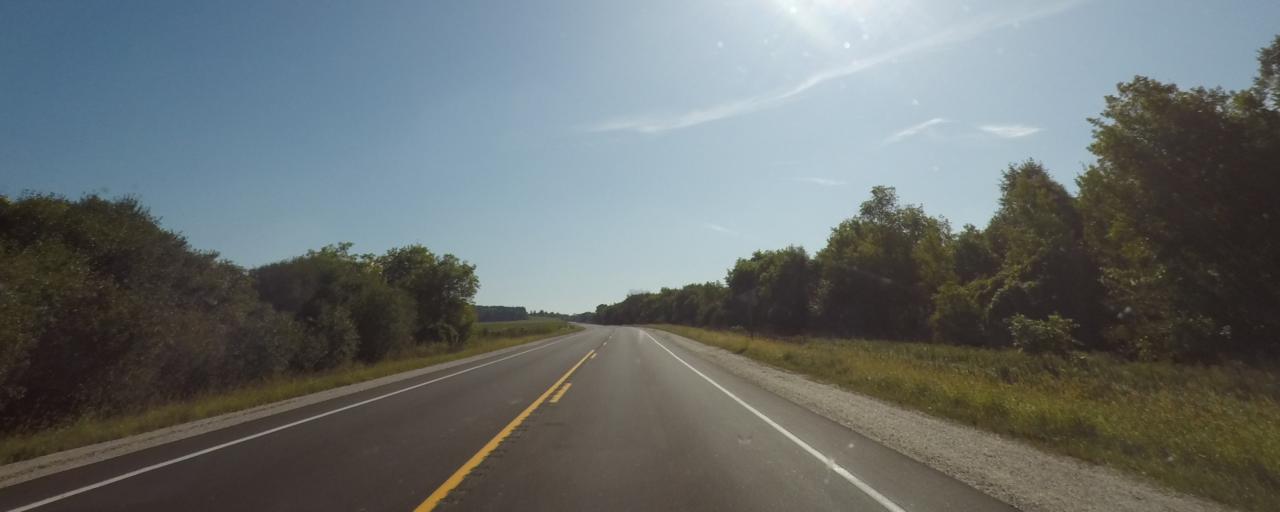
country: US
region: Wisconsin
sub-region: Jefferson County
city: Ixonia
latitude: 43.0130
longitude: -88.6334
